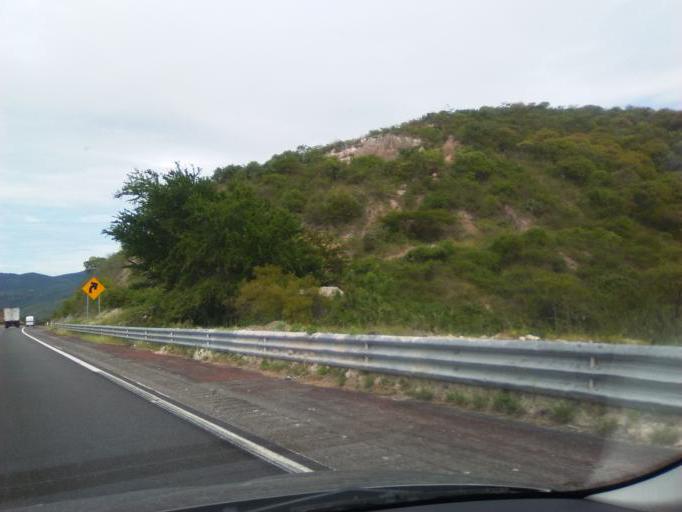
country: MX
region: Guerrero
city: Zumpango del Rio
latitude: 17.6207
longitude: -99.5176
